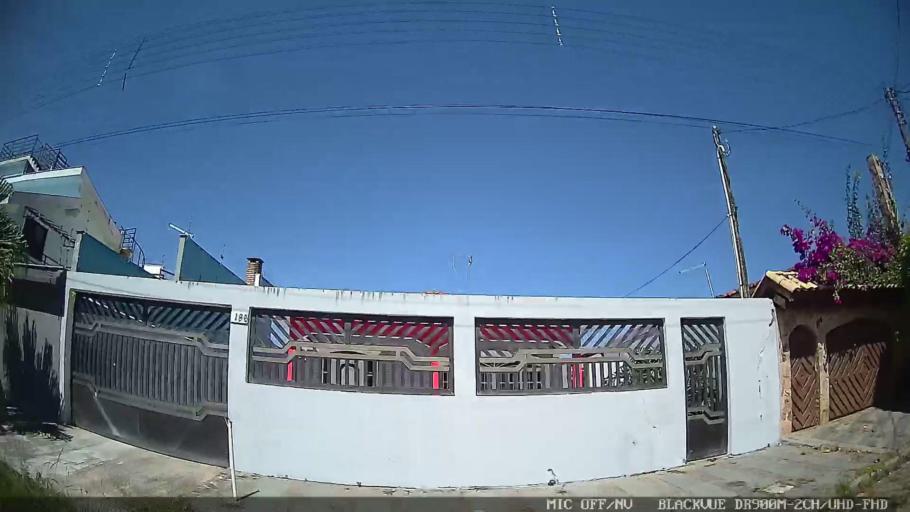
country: BR
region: Sao Paulo
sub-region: Peruibe
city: Peruibe
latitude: -24.3054
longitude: -46.9788
